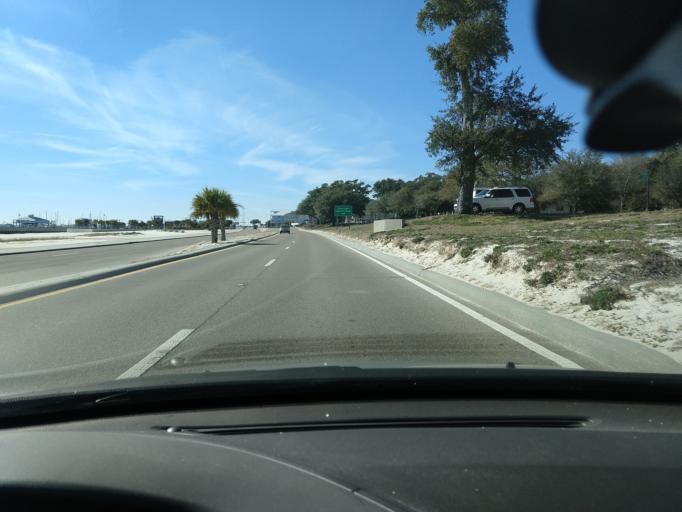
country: US
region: Mississippi
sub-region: Harrison County
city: Pass Christian
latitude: 30.3167
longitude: -89.2394
